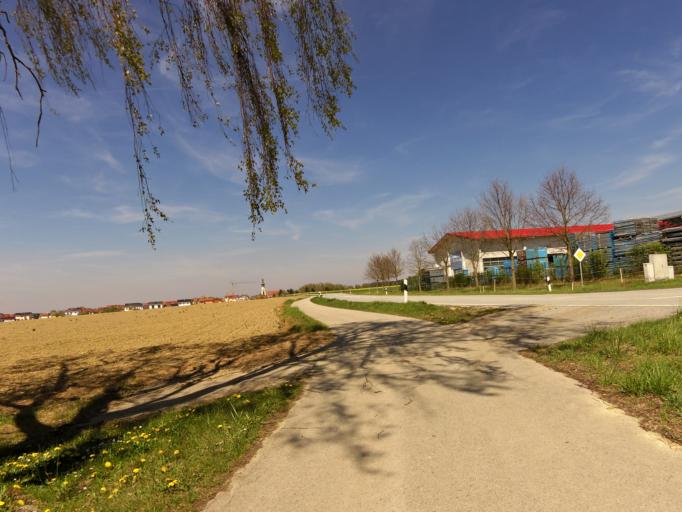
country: DE
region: Bavaria
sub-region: Upper Bavaria
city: Bockhorn
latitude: 48.3069
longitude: 11.9857
